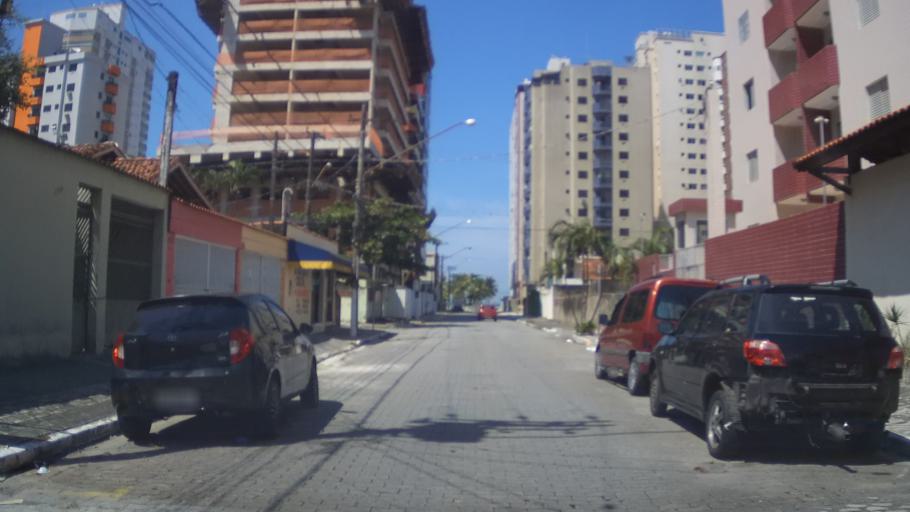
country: BR
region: Sao Paulo
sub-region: Praia Grande
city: Praia Grande
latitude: -24.0164
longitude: -46.4408
